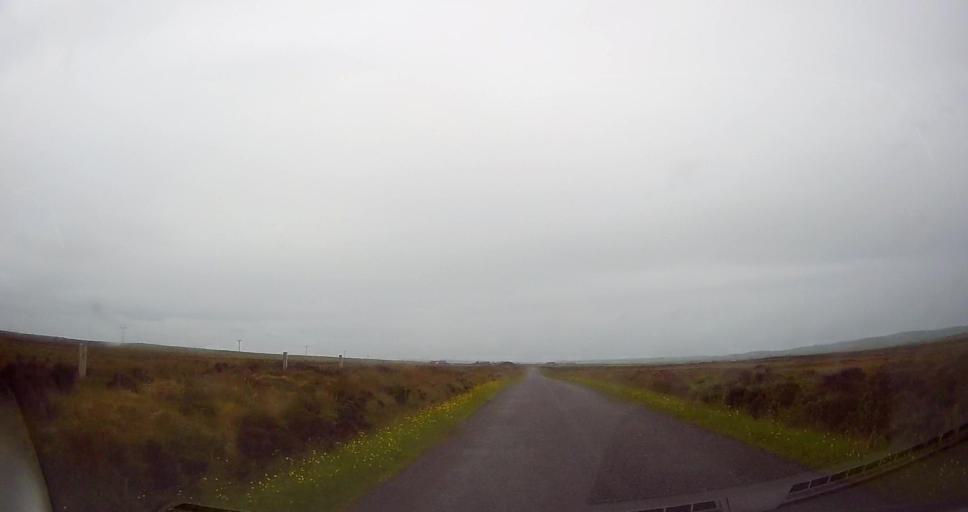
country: GB
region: Scotland
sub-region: Orkney Islands
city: Stromness
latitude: 59.0818
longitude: -3.1924
